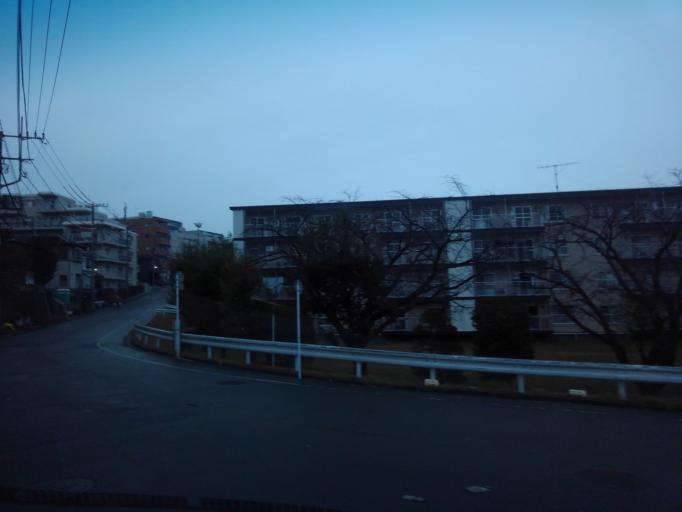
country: JP
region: Tokyo
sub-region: Machida-shi
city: Machida
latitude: 35.5452
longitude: 139.4354
